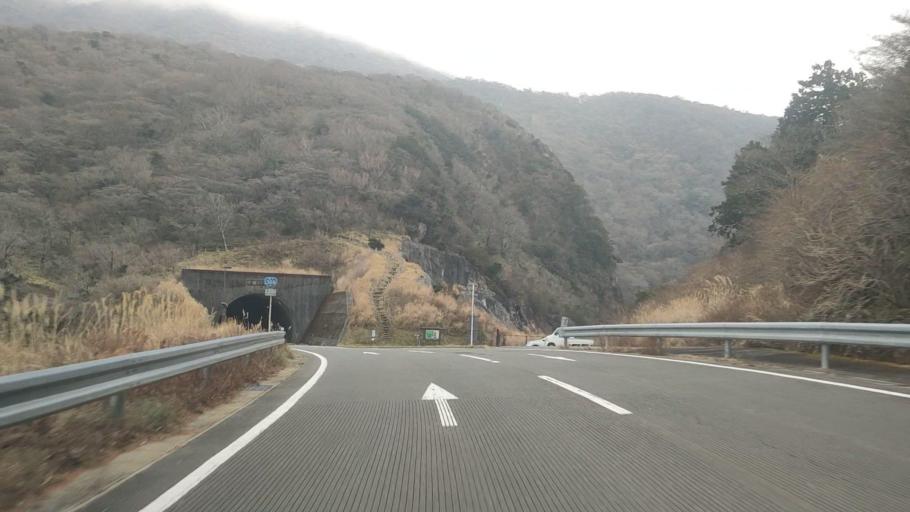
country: JP
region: Nagasaki
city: Shimabara
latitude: 32.7634
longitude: 130.2747
